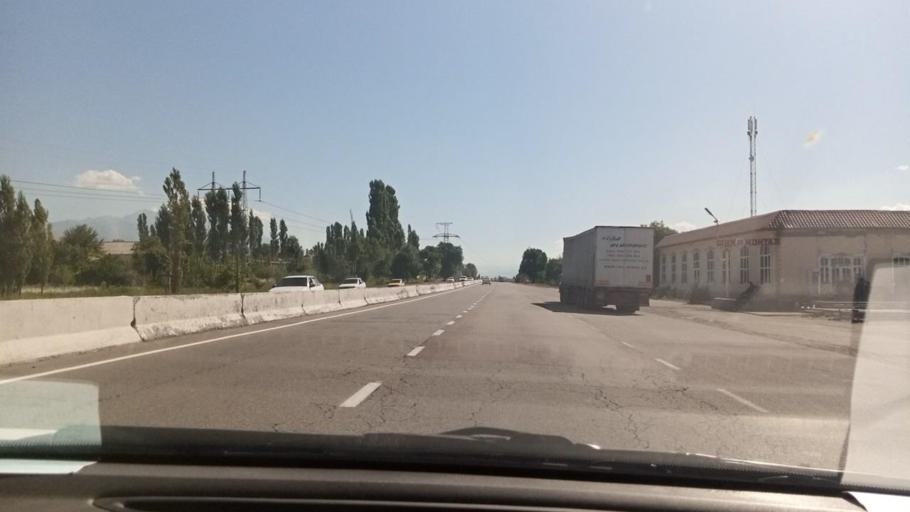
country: UZ
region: Toshkent
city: Angren
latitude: 40.9853
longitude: 70.0299
